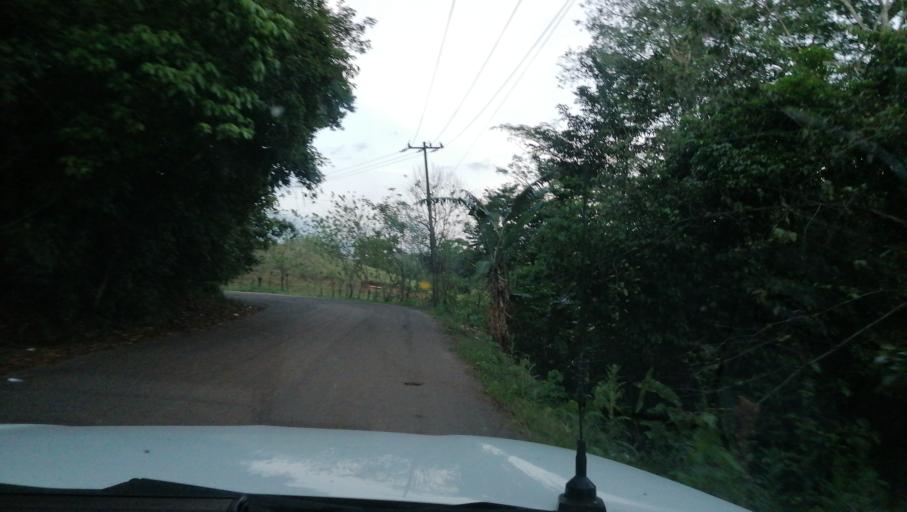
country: MX
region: Chiapas
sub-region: Ostuacan
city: Nuevo Juan del Grijalva
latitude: 17.4449
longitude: -93.3536
